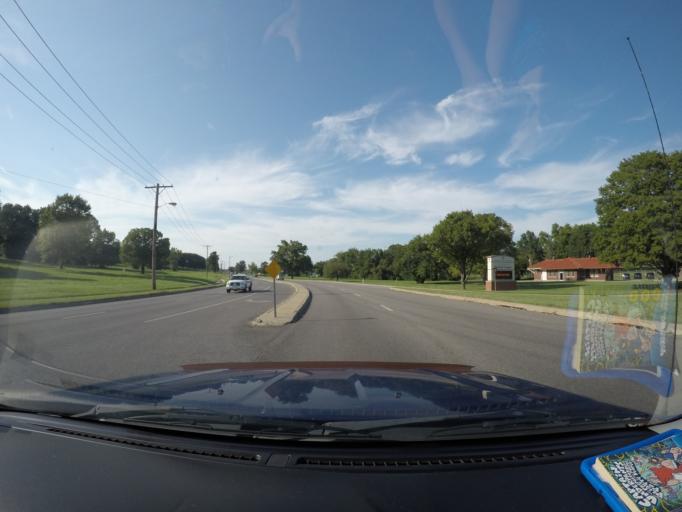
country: US
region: Kansas
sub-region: Leavenworth County
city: Lansing
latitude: 39.2776
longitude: -94.8998
